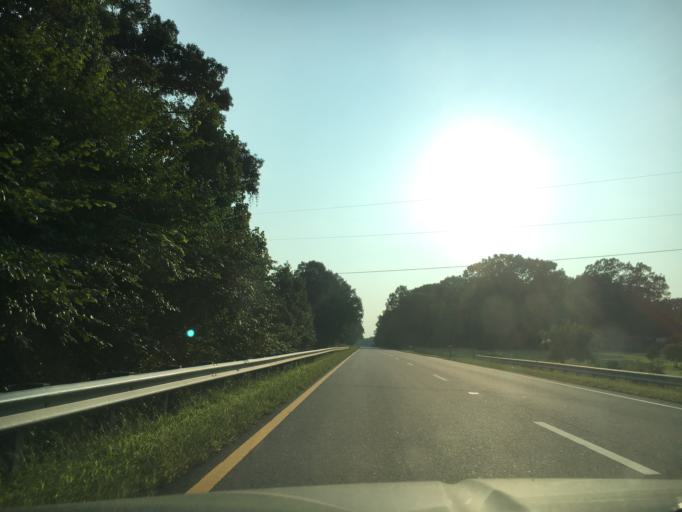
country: US
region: Virginia
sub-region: Prince Edward County
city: Hampden Sydney
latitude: 37.2952
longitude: -78.5923
